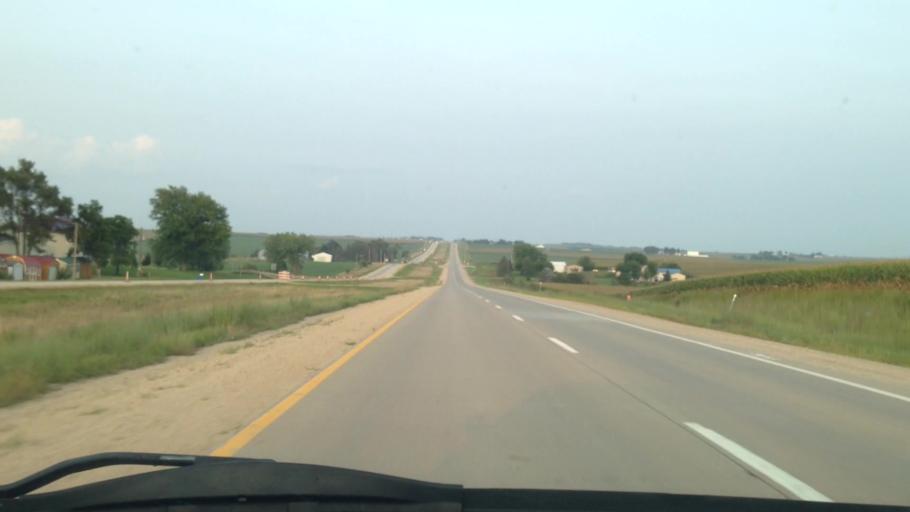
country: US
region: Iowa
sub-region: Benton County
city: Atkins
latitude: 41.9633
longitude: -91.9980
